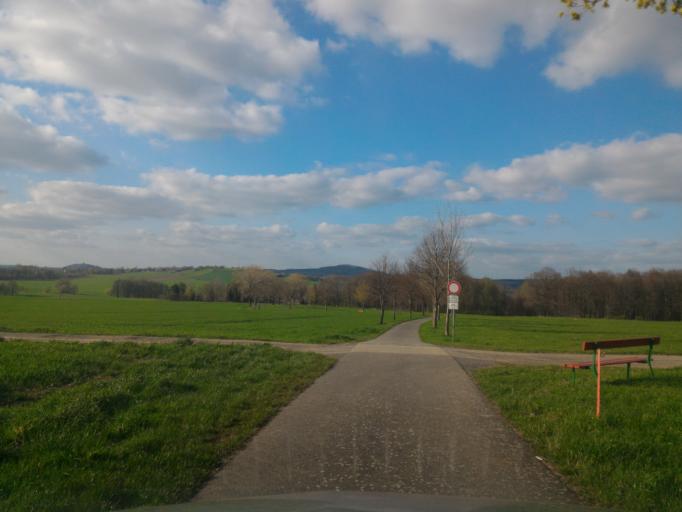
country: CZ
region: Ustecky
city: Varnsdorf
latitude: 50.8764
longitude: 14.6448
